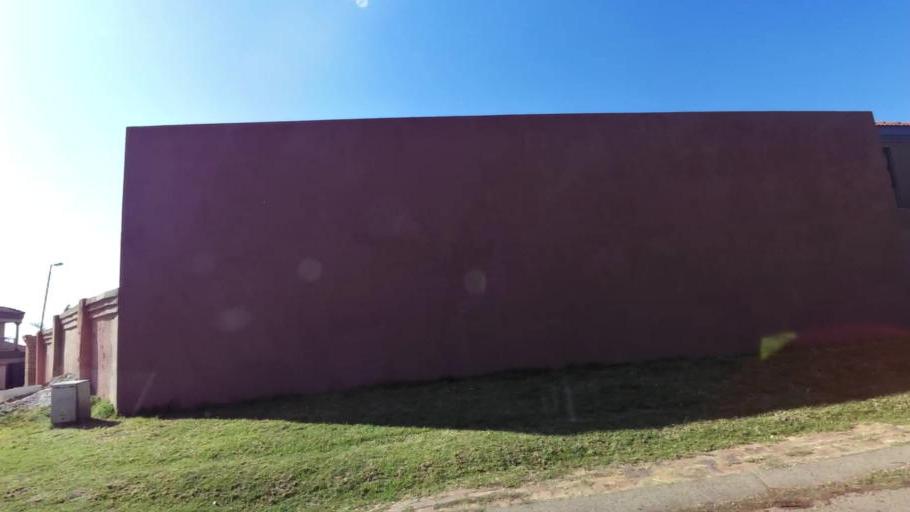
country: ZA
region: Gauteng
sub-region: City of Johannesburg Metropolitan Municipality
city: Johannesburg
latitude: -26.2531
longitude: 27.9860
